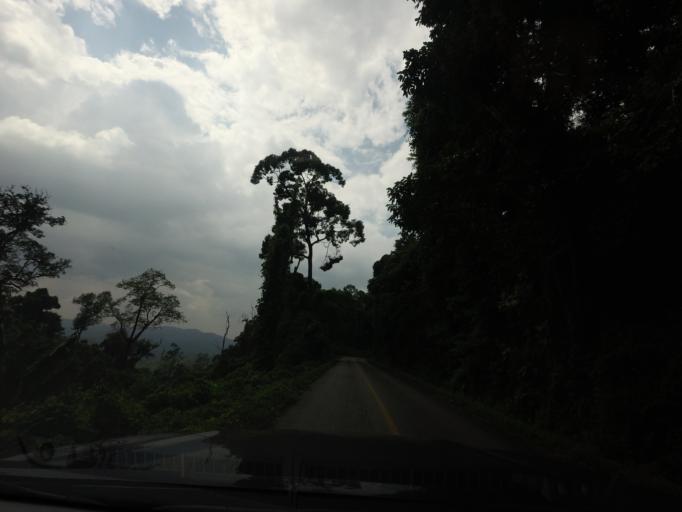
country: TH
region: Uttaradit
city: Nam Pat
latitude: 17.7217
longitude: 100.9479
